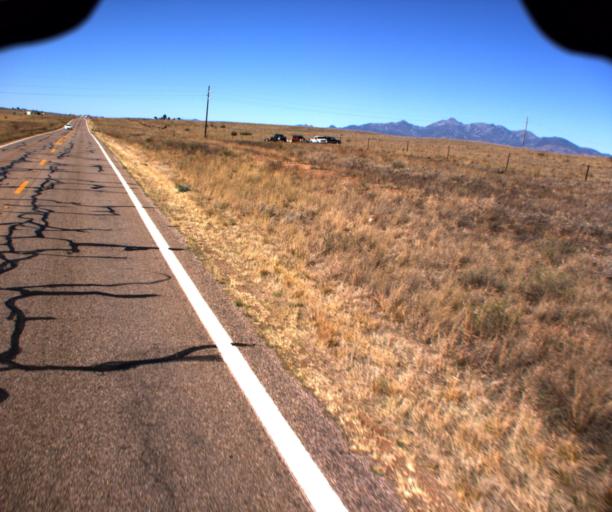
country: US
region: Arizona
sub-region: Cochise County
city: Huachuca City
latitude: 31.6928
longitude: -110.6067
